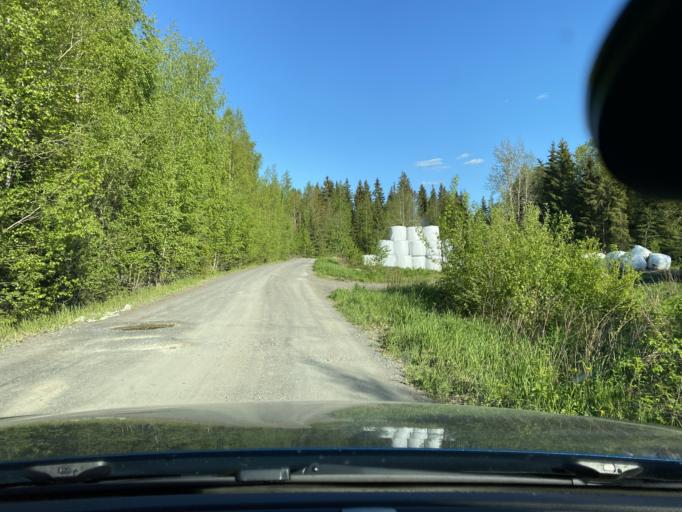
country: FI
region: Pirkanmaa
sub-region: Lounais-Pirkanmaa
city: Punkalaidun
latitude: 61.0752
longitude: 23.0814
